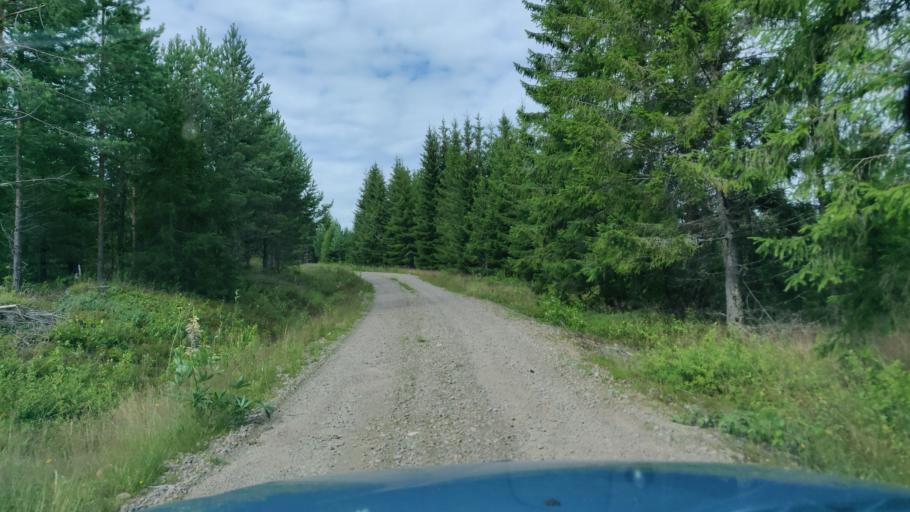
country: SE
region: Vaermland
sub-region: Hagfors Kommun
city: Hagfors
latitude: 59.9456
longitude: 13.5968
